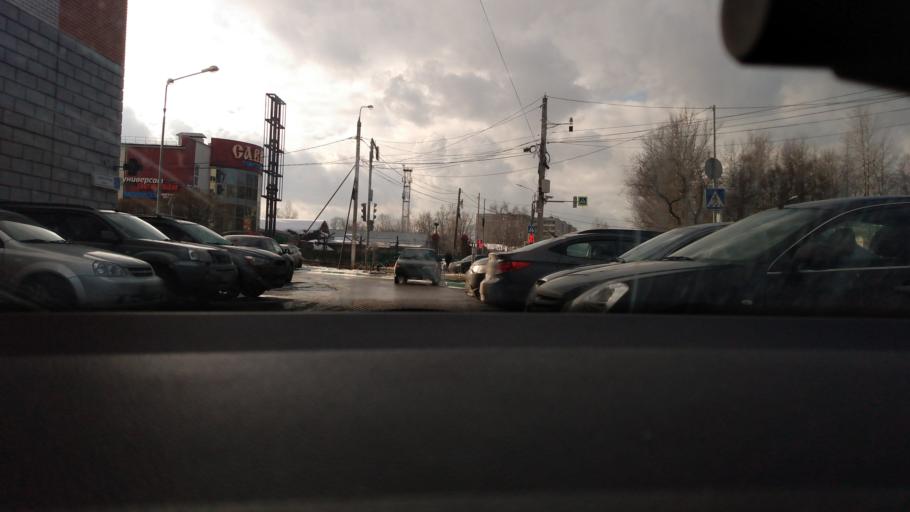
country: RU
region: Moskovskaya
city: Zheleznodorozhnyy
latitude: 55.7301
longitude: 38.0297
